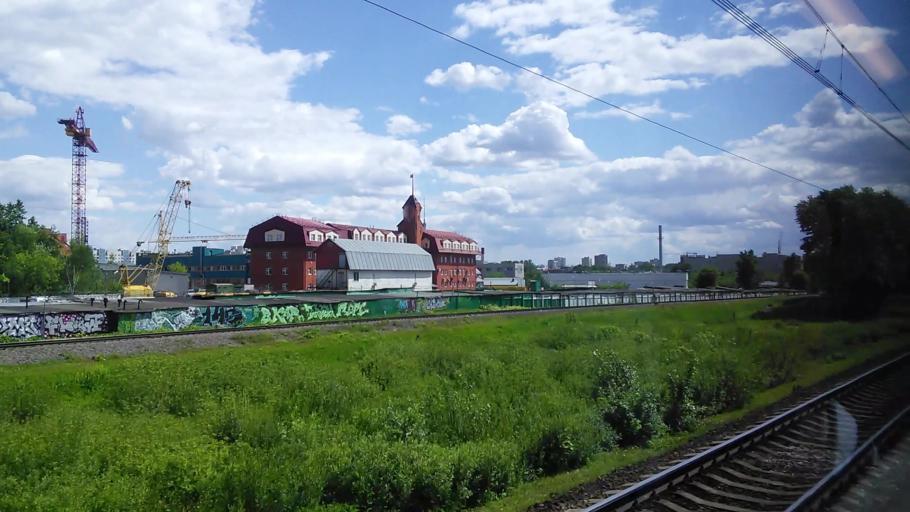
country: RU
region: Moscow
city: Likhobory
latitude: 55.8586
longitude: 37.5743
